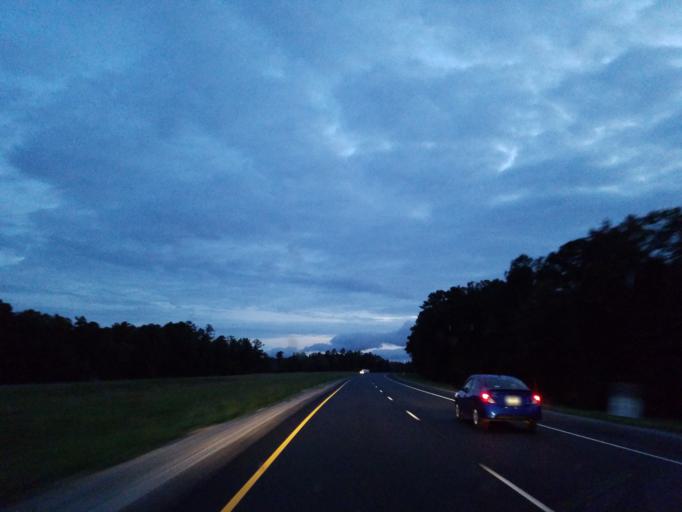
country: US
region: Mississippi
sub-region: Clarke County
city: Stonewall
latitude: 32.0191
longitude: -88.9241
